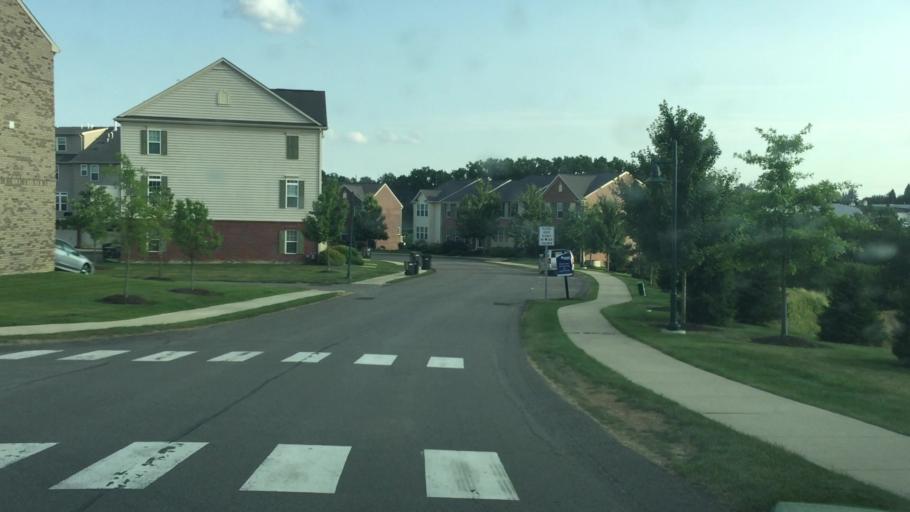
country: US
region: Pennsylvania
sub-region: Allegheny County
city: Bradford Woods
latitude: 40.6310
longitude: -80.0532
